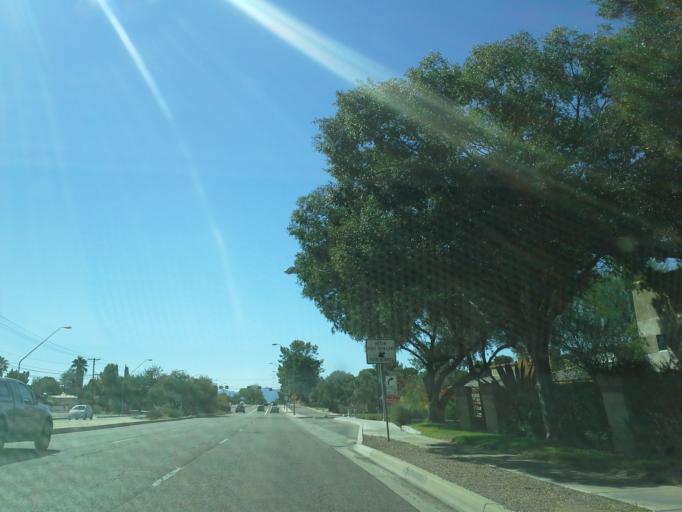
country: US
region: Arizona
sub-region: Pima County
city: Tucson
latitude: 32.2508
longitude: -110.8640
